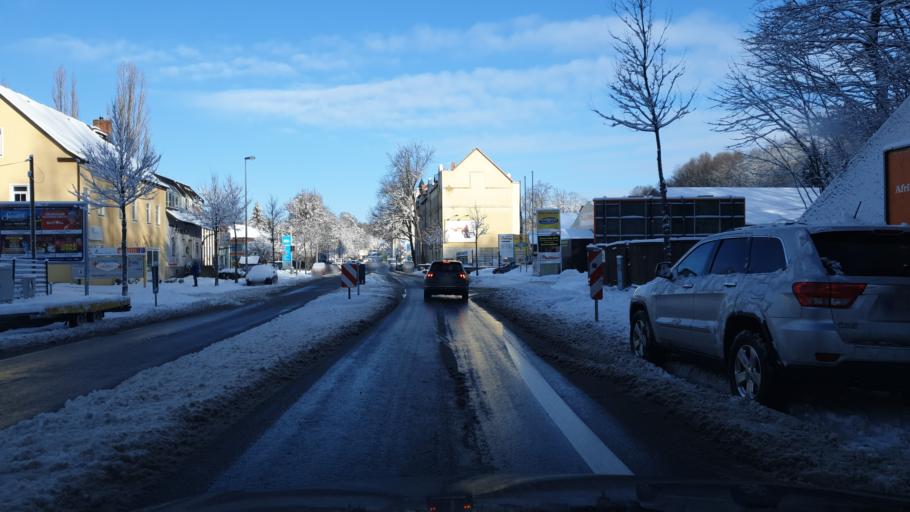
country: DE
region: Saxony
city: Chemnitz
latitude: 50.8543
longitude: 12.9295
